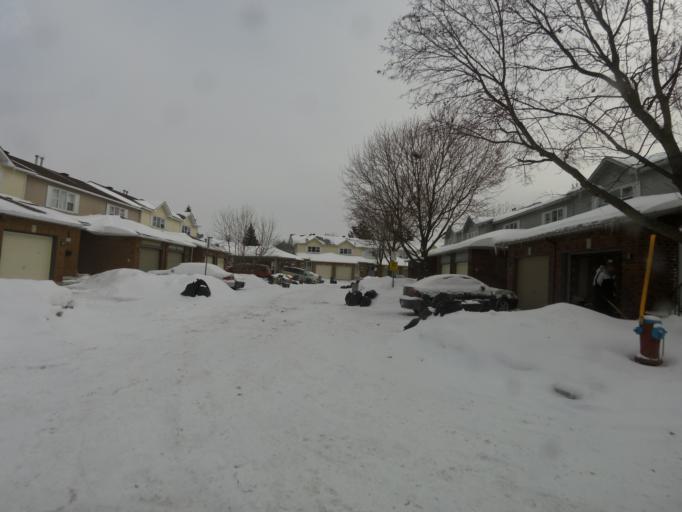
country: CA
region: Ontario
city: Ottawa
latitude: 45.3729
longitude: -75.6039
